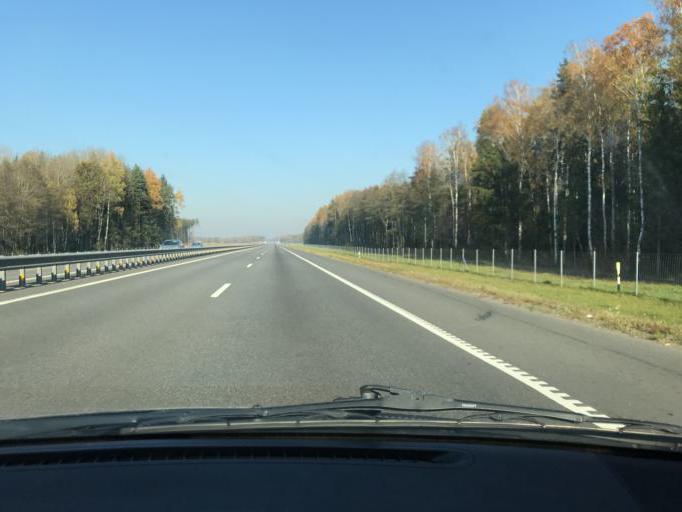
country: BY
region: Minsk
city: Slutsk
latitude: 53.2590
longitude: 27.5503
